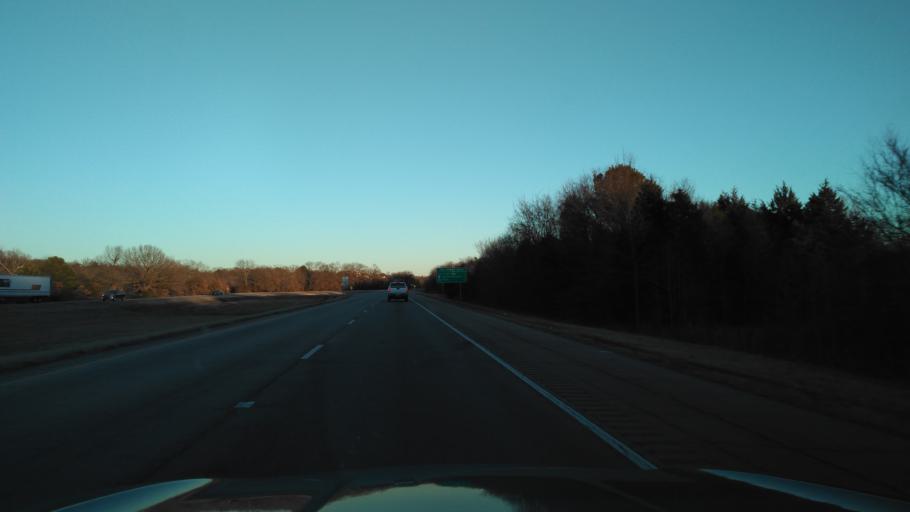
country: US
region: Arkansas
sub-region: Crawford County
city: Van Buren
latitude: 35.4627
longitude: -94.4133
